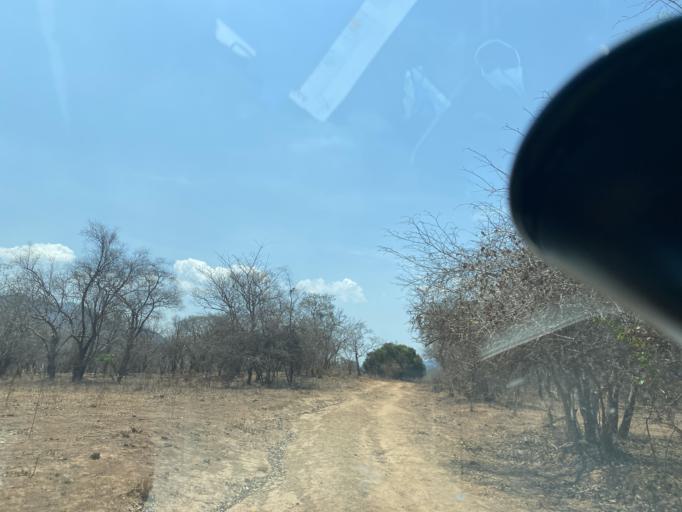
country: ZM
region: Lusaka
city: Kafue
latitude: -15.7822
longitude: 28.4602
